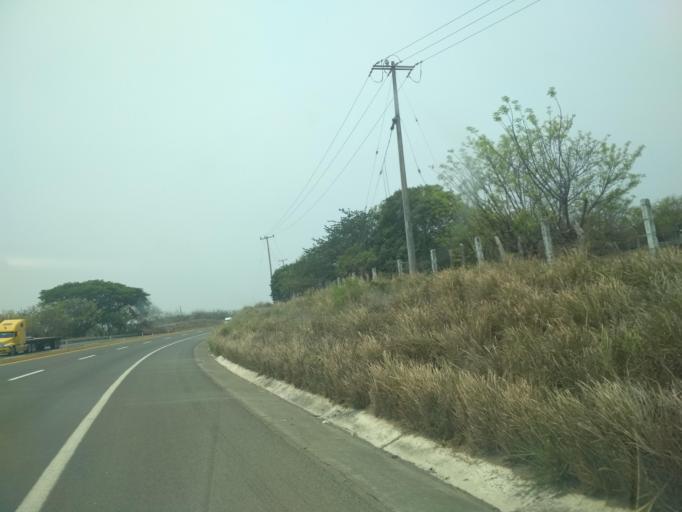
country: MX
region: Veracruz
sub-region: Veracruz
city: Delfino Victoria (Santa Fe)
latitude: 19.2110
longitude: -96.2600
